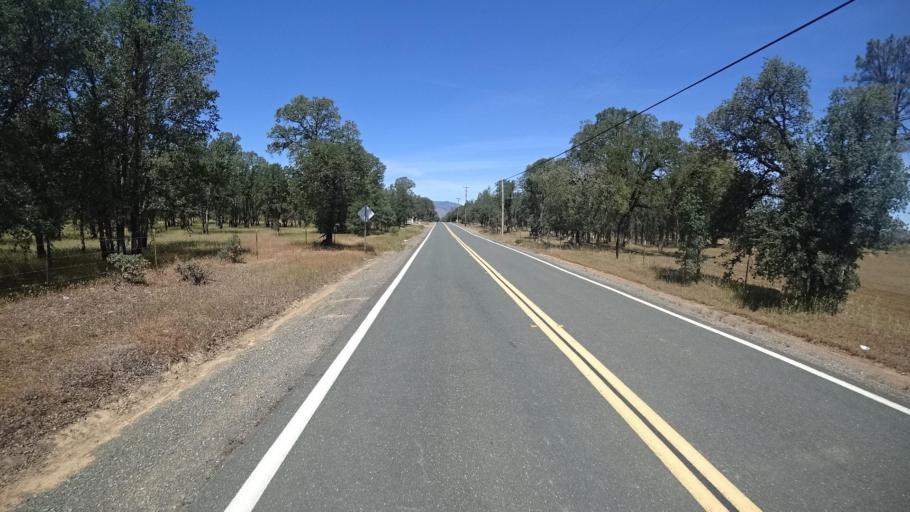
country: US
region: California
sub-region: Lake County
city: Middletown
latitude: 38.7245
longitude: -122.5472
